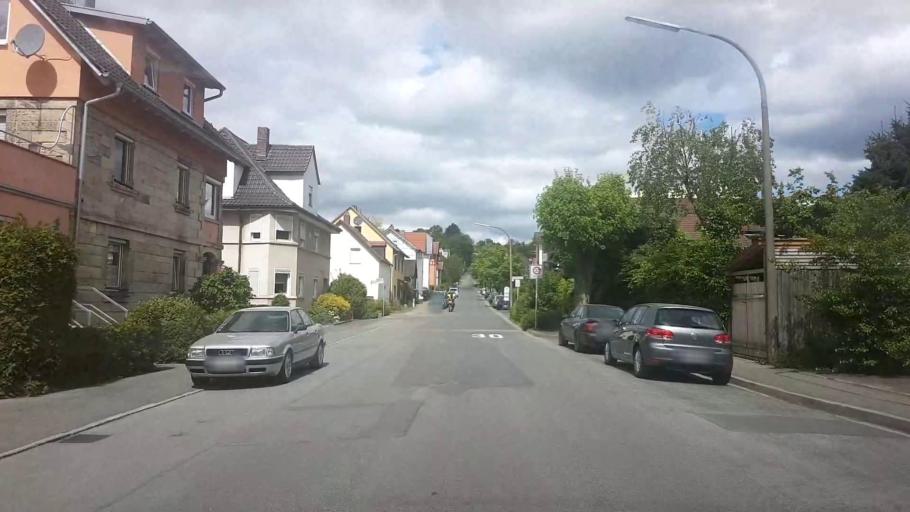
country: DE
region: Bavaria
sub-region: Upper Franconia
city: Lichtenfels
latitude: 50.1530
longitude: 11.0579
